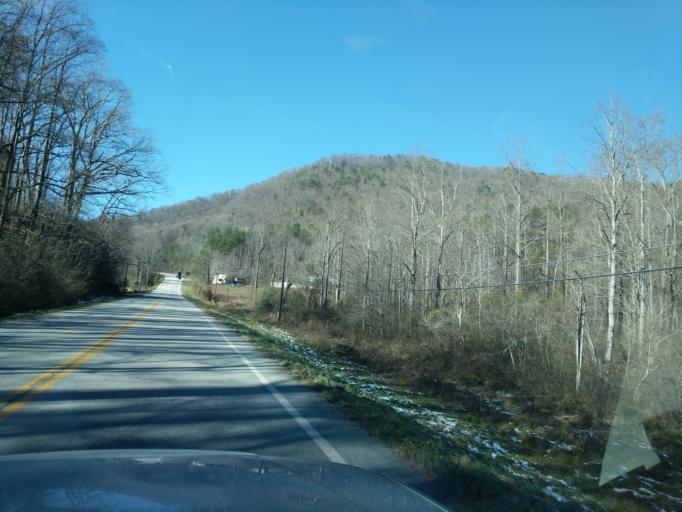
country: US
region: Georgia
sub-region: Rabun County
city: Clayton
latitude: 34.8594
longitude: -83.3714
